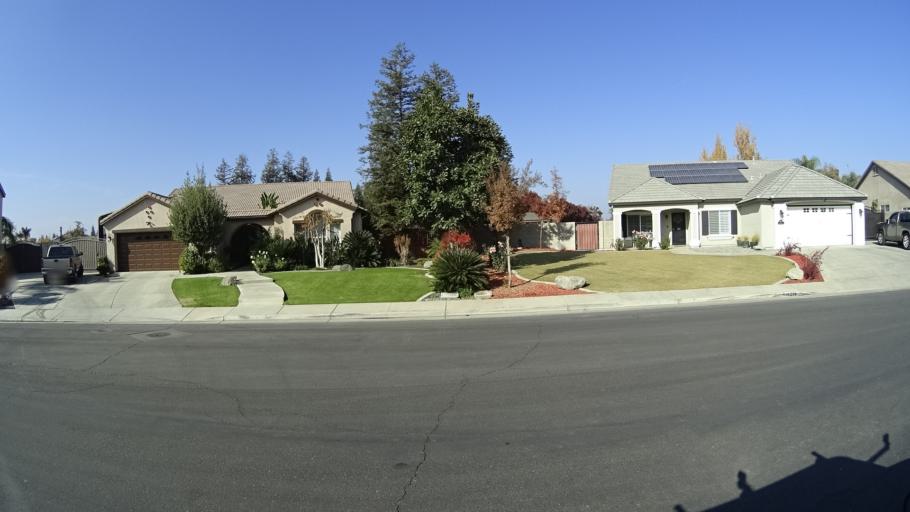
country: US
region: California
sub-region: Kern County
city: Rosedale
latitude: 35.3610
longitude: -119.1713
